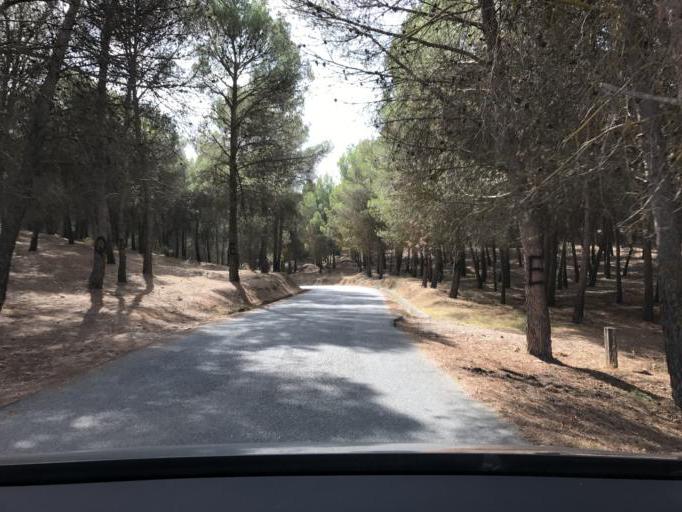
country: ES
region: Andalusia
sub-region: Provincia de Granada
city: Jun
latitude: 37.1940
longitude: -3.5707
